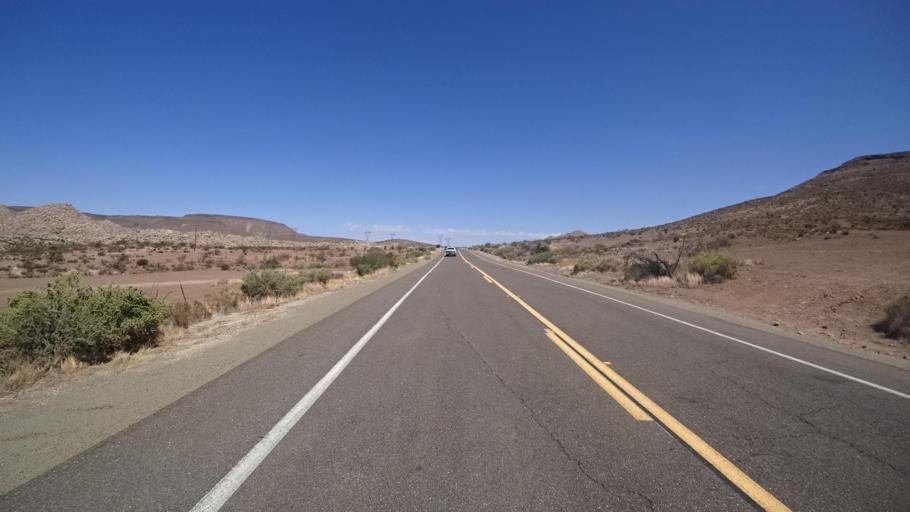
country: MX
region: Baja California
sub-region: Tecate
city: Cereso del Hongo
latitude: 32.6242
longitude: -116.1517
